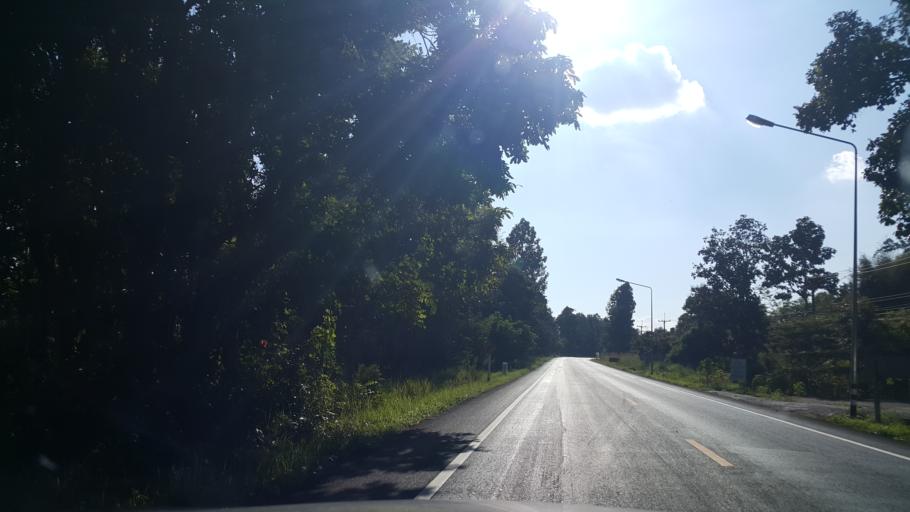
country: TH
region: Lamphun
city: Mae Tha
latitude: 18.4700
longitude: 99.1572
